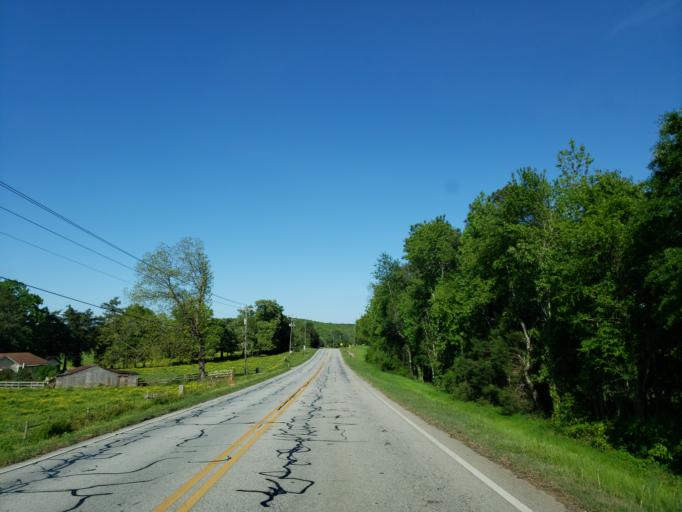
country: US
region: Georgia
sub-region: Polk County
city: Cedartown
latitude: 33.9105
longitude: -85.3046
